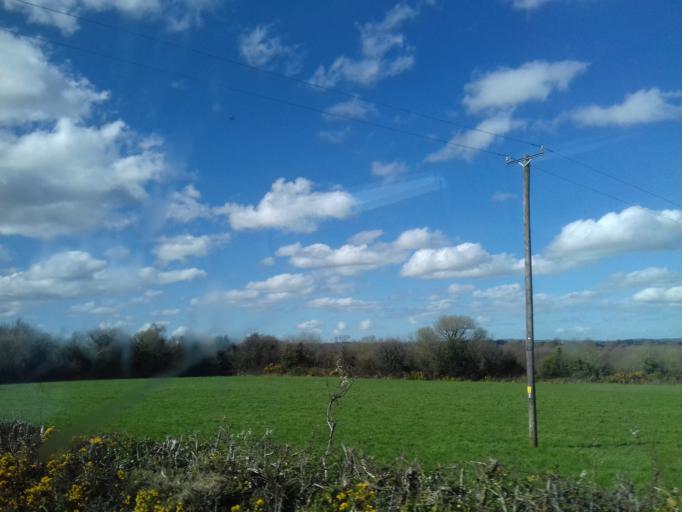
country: IE
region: Munster
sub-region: County Cork
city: Kanturk
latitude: 52.1284
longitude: -8.8267
